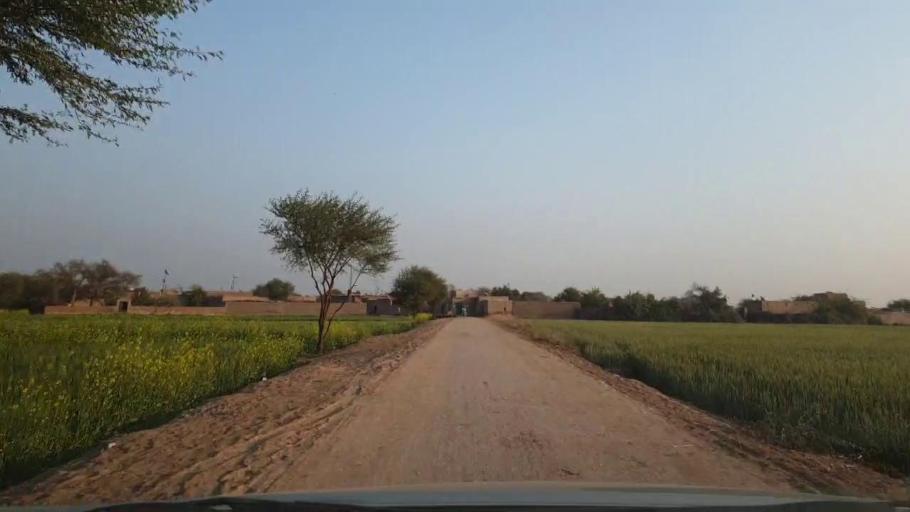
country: PK
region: Sindh
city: Tando Adam
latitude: 25.7052
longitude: 68.6052
